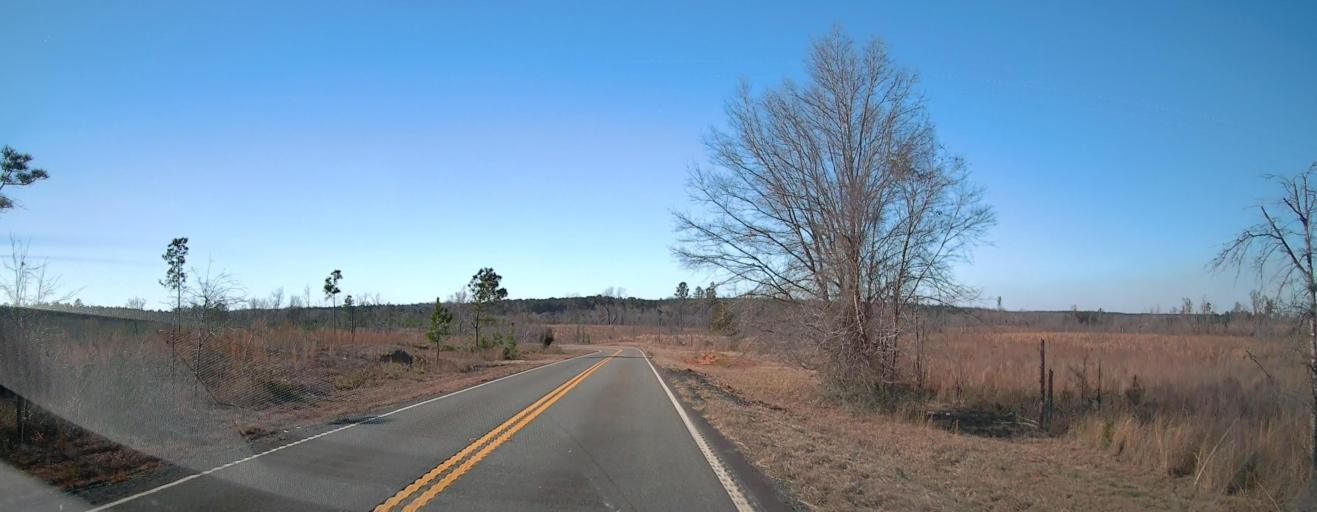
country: US
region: Georgia
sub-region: Talbot County
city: Talbotton
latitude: 32.6487
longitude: -84.4042
